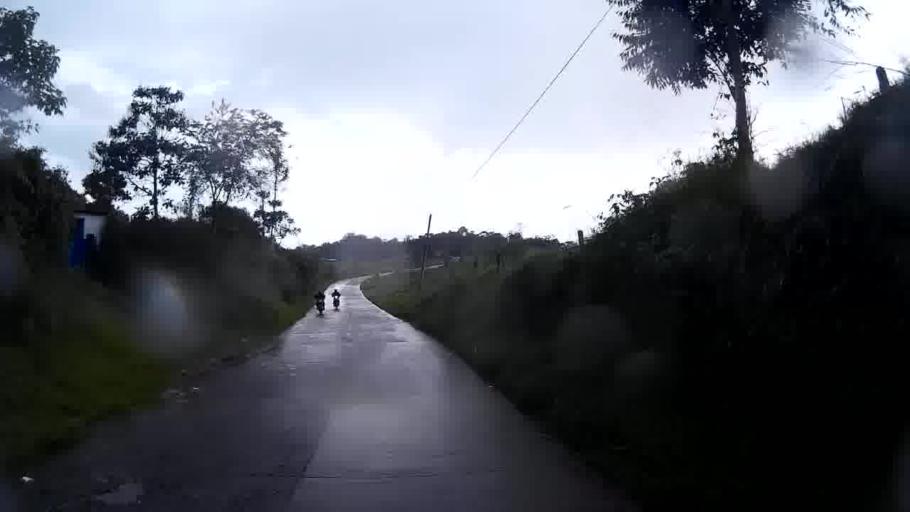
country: CO
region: Quindio
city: Filandia
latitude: 4.6896
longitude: -75.6103
